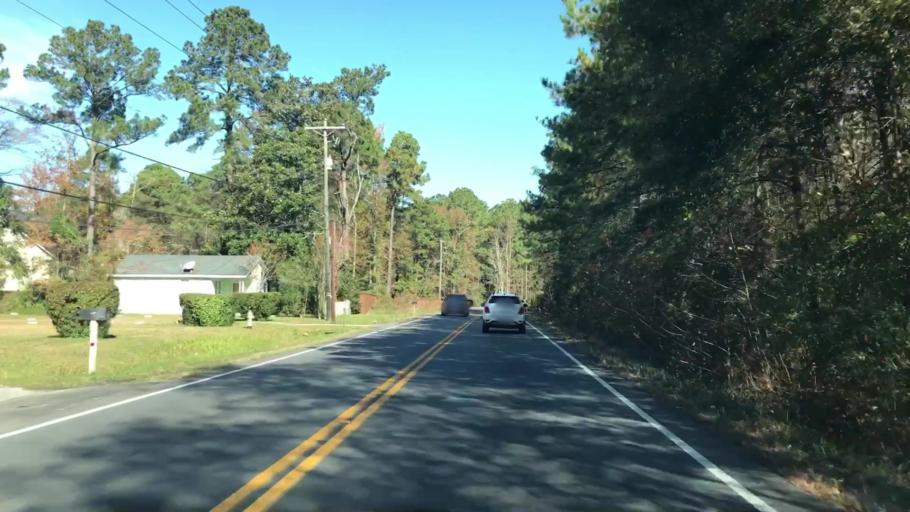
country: US
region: South Carolina
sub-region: Dorchester County
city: Summerville
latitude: 33.0210
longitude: -80.2036
